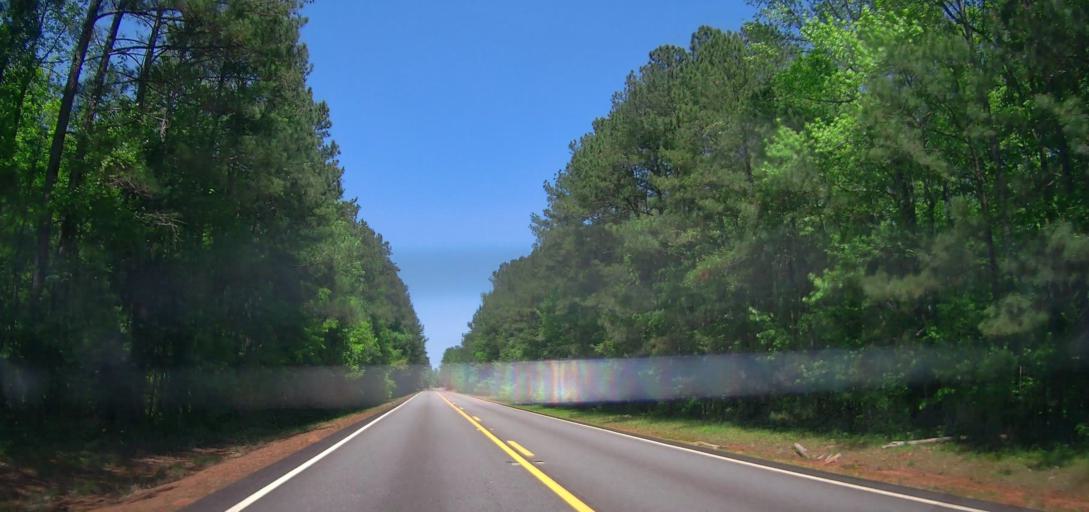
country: US
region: Georgia
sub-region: Jasper County
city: Monticello
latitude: 33.2864
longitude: -83.6464
